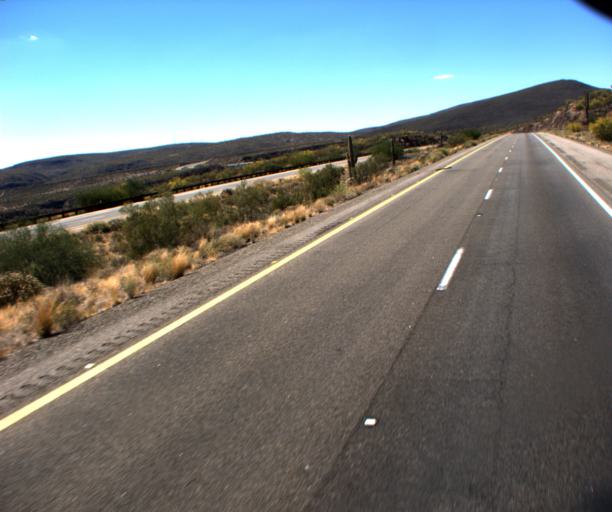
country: US
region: Arizona
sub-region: Yavapai County
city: Bagdad
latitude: 34.5388
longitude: -113.4350
